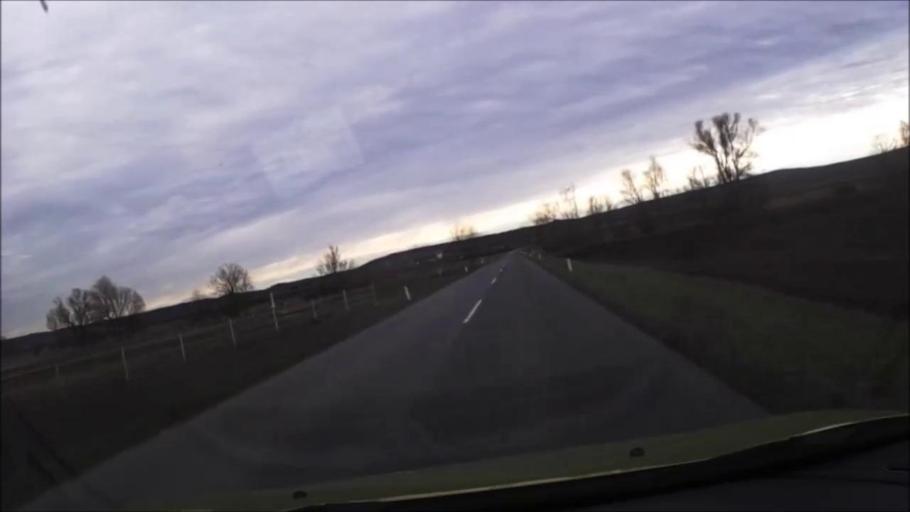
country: AT
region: Burgenland
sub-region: Eisenstadt-Umgebung
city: Leithaprodersdorf
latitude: 47.9312
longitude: 16.4951
